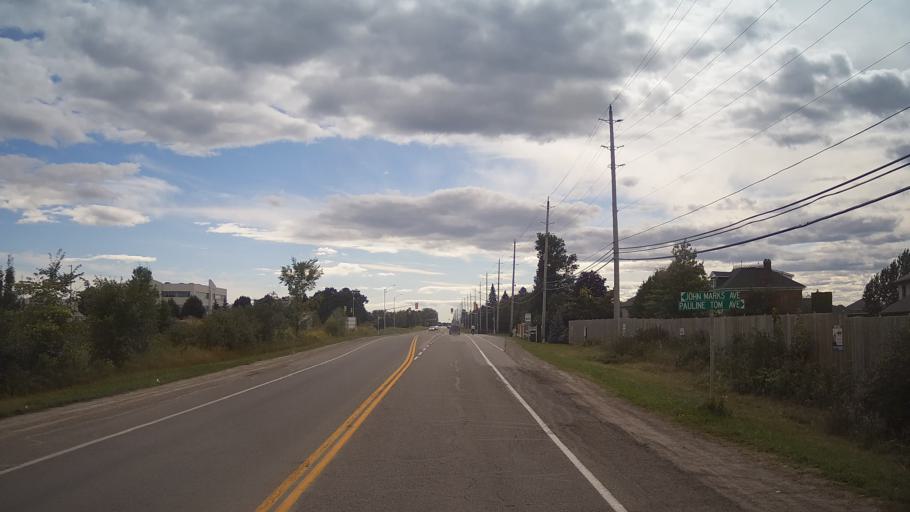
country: CA
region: Ontario
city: Kingston
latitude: 44.2769
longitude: -76.4425
